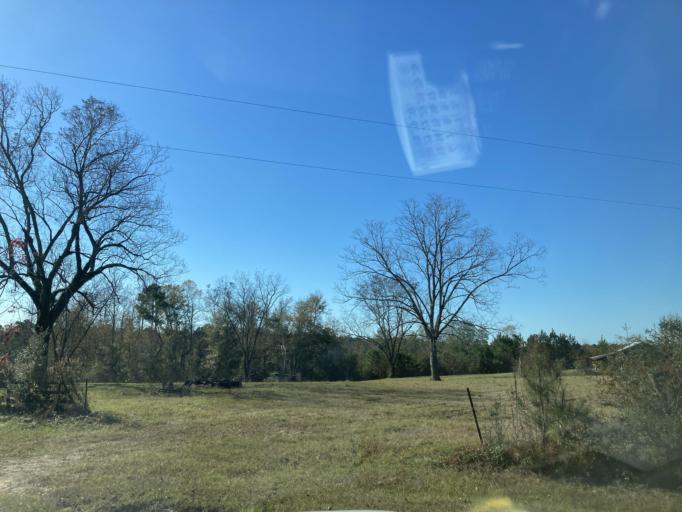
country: US
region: Mississippi
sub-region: Lamar County
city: Sumrall
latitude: 31.2924
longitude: -89.5970
